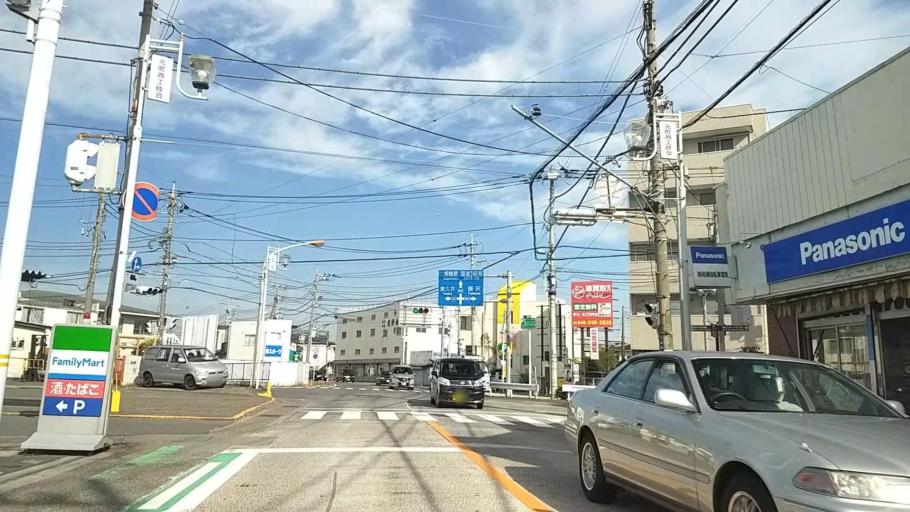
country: JP
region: Kanagawa
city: Atsugi
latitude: 35.4465
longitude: 139.3667
